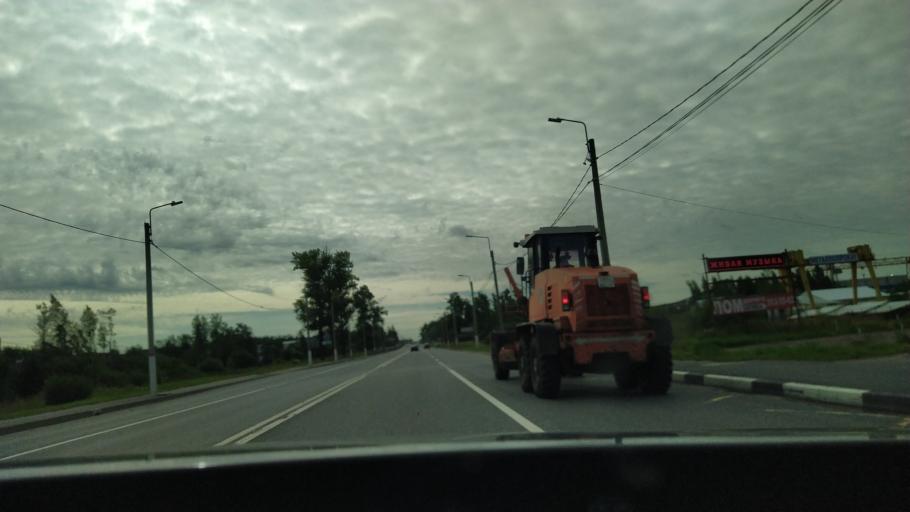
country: RU
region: Leningrad
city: Tosno
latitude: 59.5628
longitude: 30.8371
